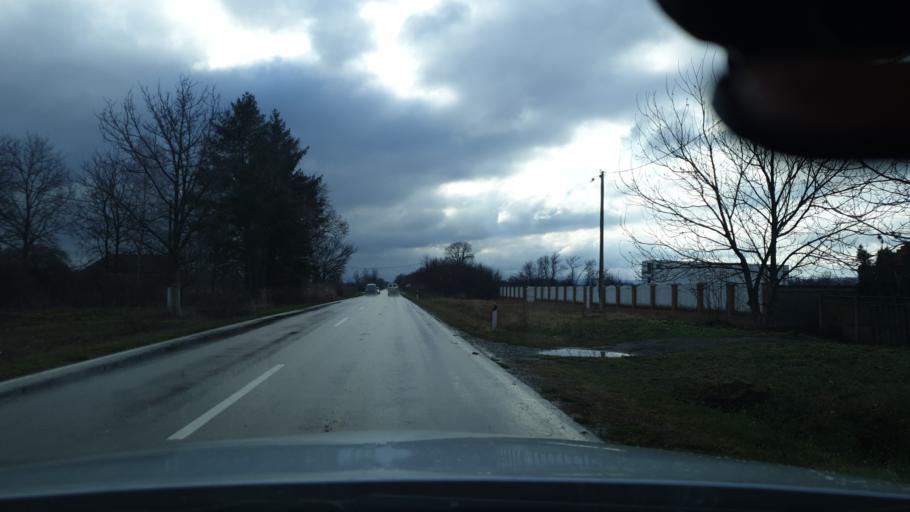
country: RS
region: Central Serbia
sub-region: Branicevski Okrug
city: Malo Crnice
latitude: 44.4993
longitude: 21.3261
